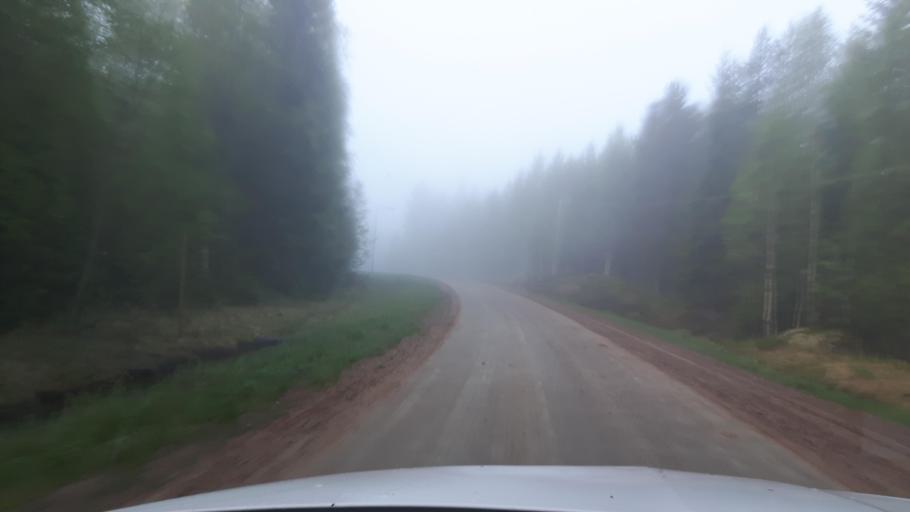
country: SE
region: Vaesternorrland
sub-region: Ange Kommun
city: Ange
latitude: 62.1454
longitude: 15.6606
